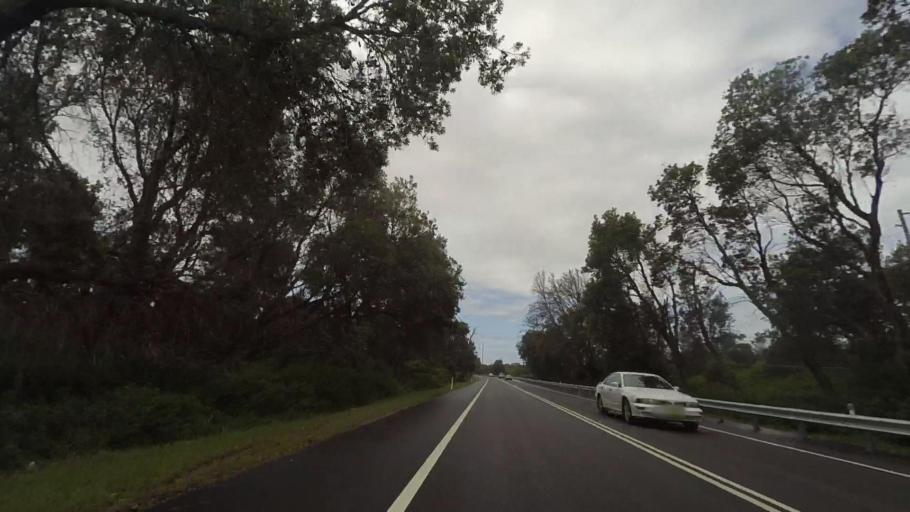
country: AU
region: New South Wales
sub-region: Wyong Shire
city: The Entrance
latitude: -33.3190
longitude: 151.5167
